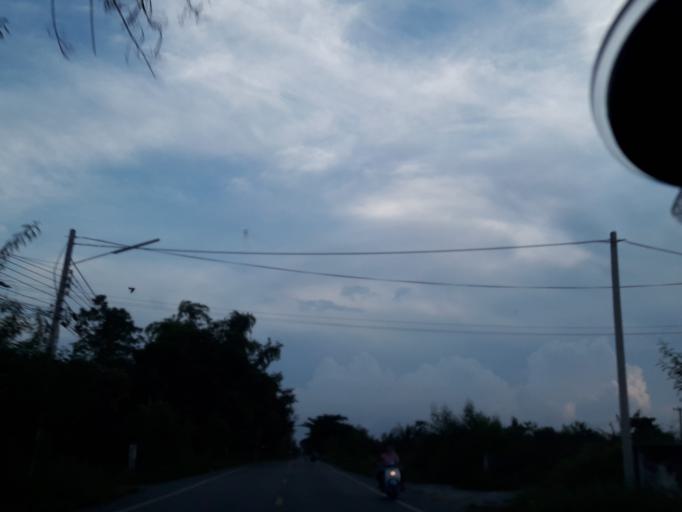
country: TH
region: Pathum Thani
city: Nong Suea
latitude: 14.1323
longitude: 100.8690
